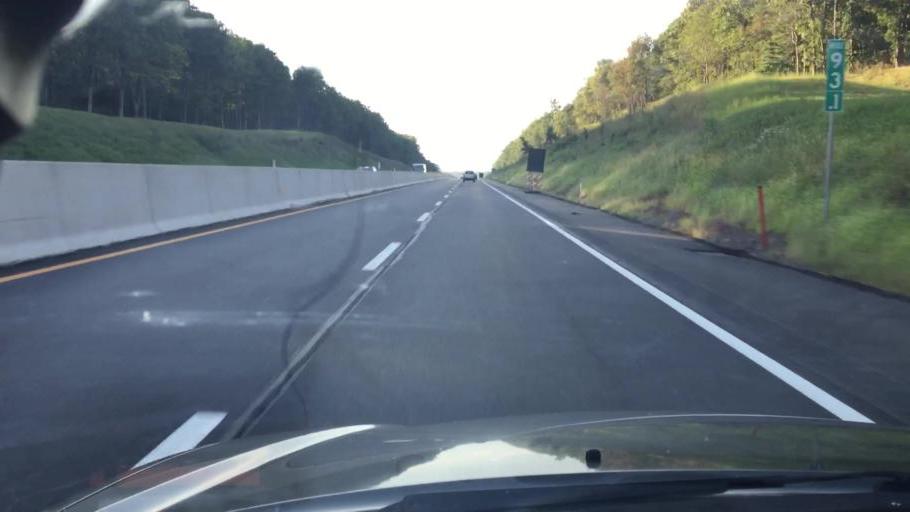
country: US
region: Pennsylvania
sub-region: Luzerne County
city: White Haven
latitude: 41.0585
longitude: -75.6834
